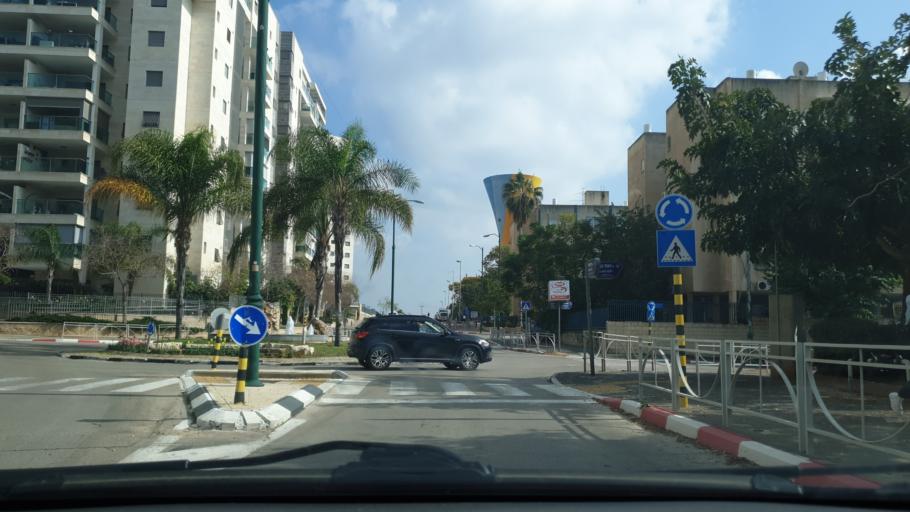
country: IL
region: Central District
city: Bet Dagan
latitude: 31.9678
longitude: 34.8228
